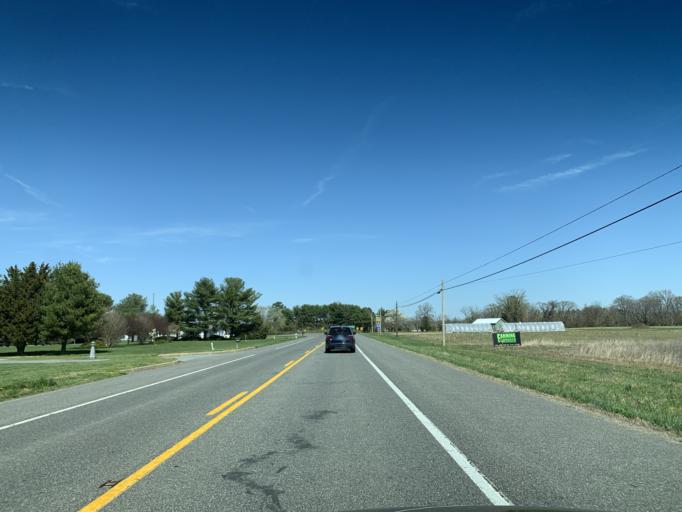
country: US
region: Maryland
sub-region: Caroline County
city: Denton
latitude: 38.8843
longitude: -75.8476
